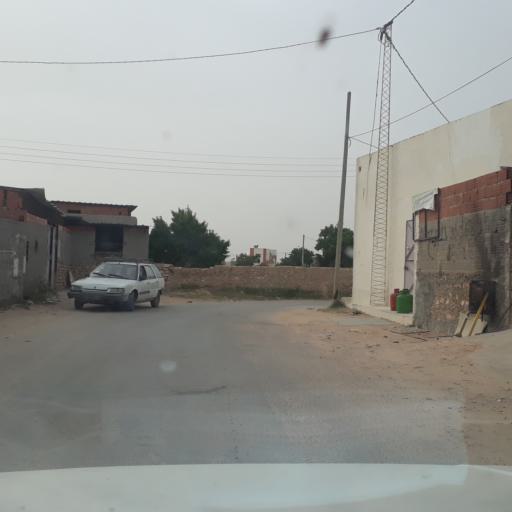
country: TN
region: Safaqis
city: Al Qarmadah
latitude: 34.8226
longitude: 10.7715
